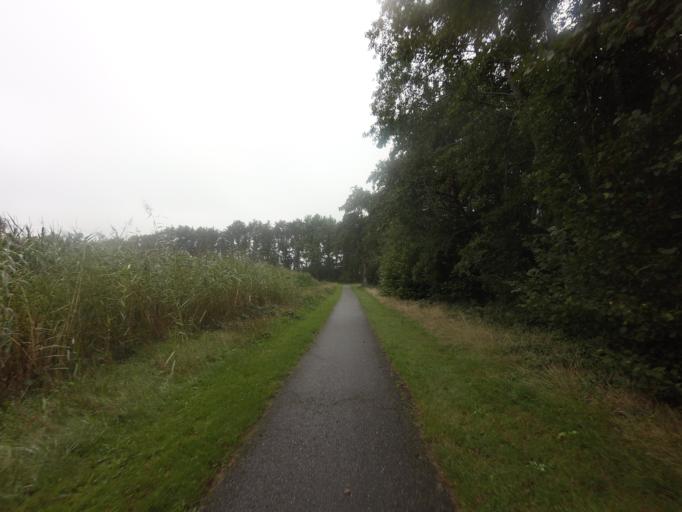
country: NL
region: Friesland
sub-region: Gemeente Heerenveen
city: Nieuwehorne
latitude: 52.9565
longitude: 6.0484
